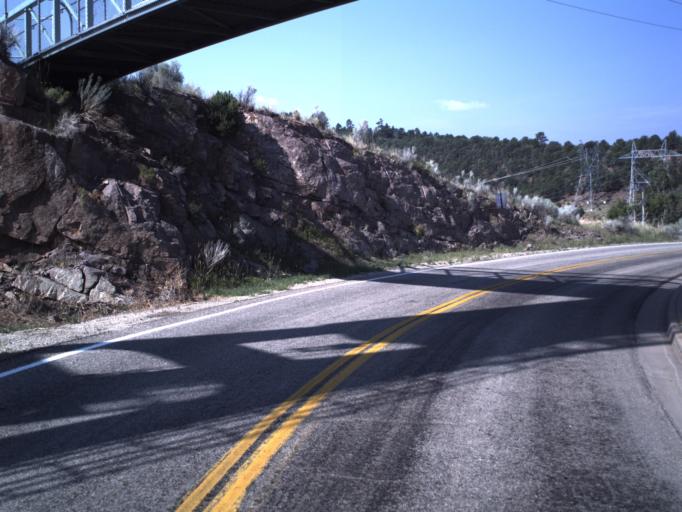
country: US
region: Utah
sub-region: Daggett County
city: Manila
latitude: 40.9140
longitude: -109.4234
